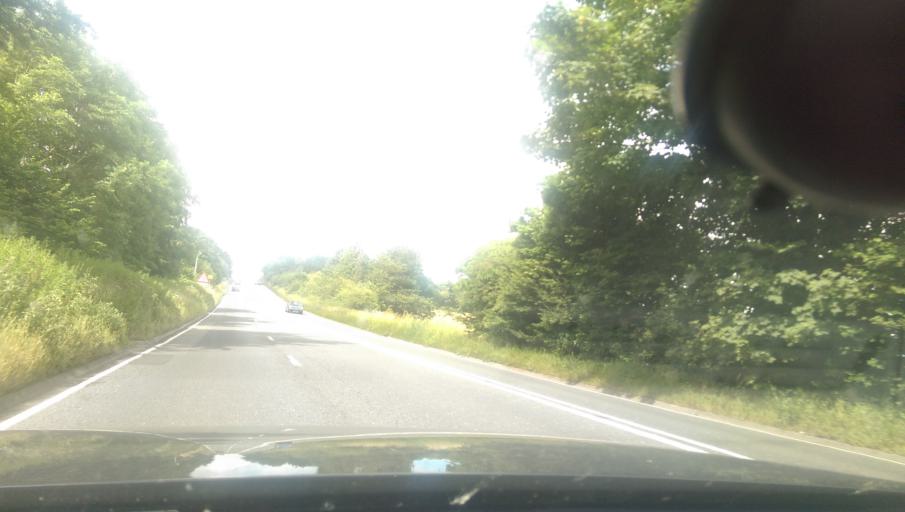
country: GB
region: England
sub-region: Wiltshire
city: Chicklade
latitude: 51.1074
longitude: -2.1472
